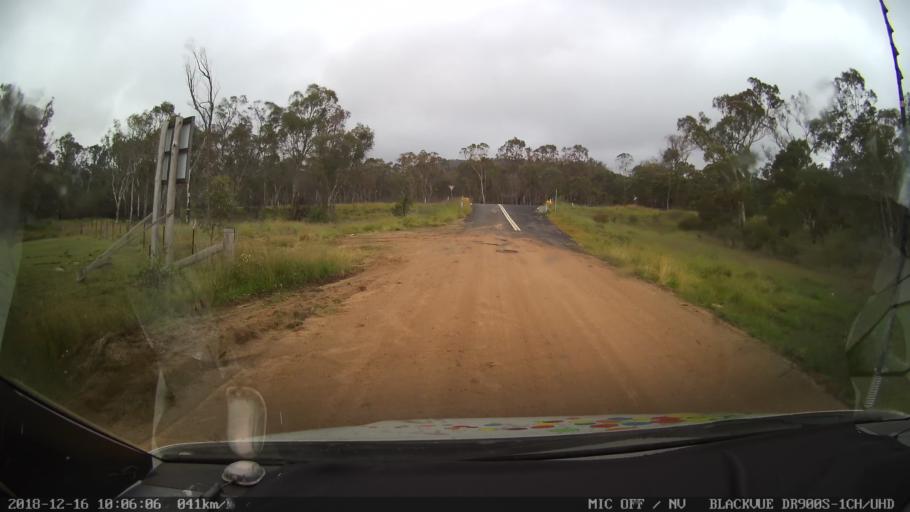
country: AU
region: New South Wales
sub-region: Glen Innes Severn
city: Glen Innes
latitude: -29.3464
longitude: 151.8914
